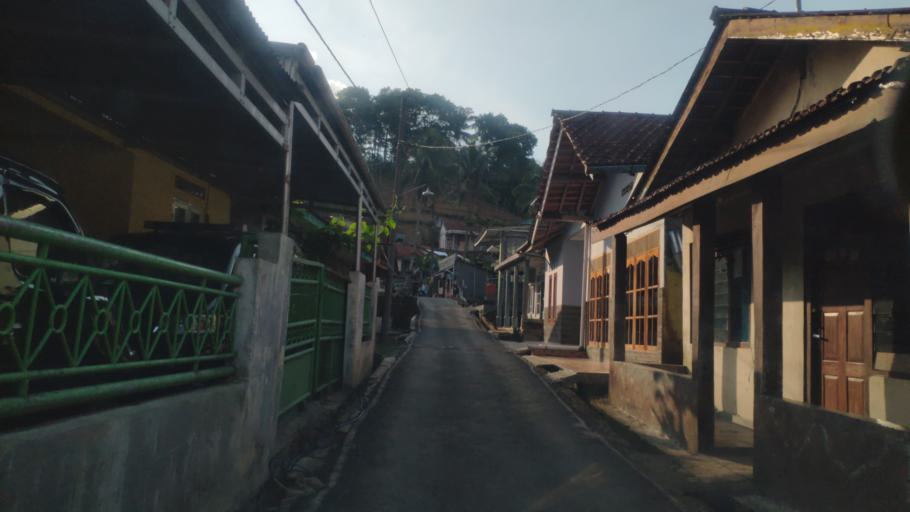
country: ID
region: Central Java
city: Buaran
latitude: -7.2437
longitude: 109.5794
